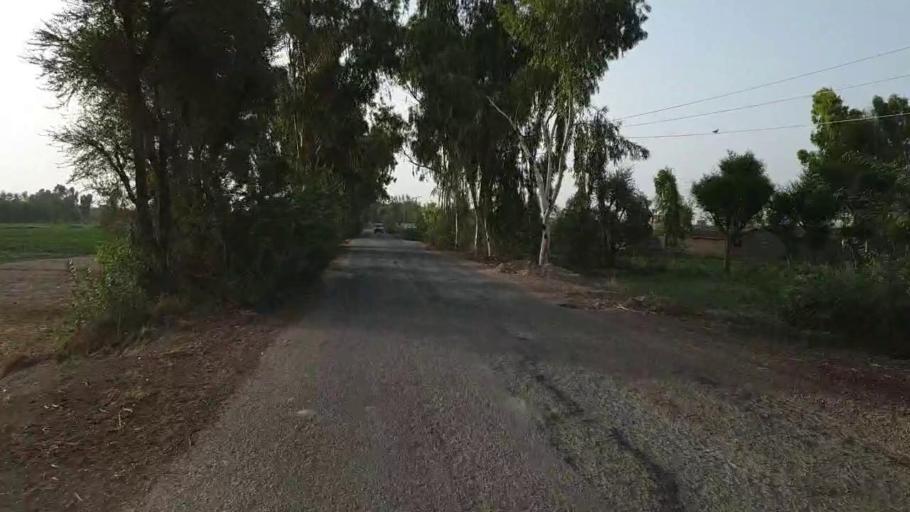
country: PK
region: Sindh
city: Bozdar
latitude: 27.1167
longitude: 68.9573
